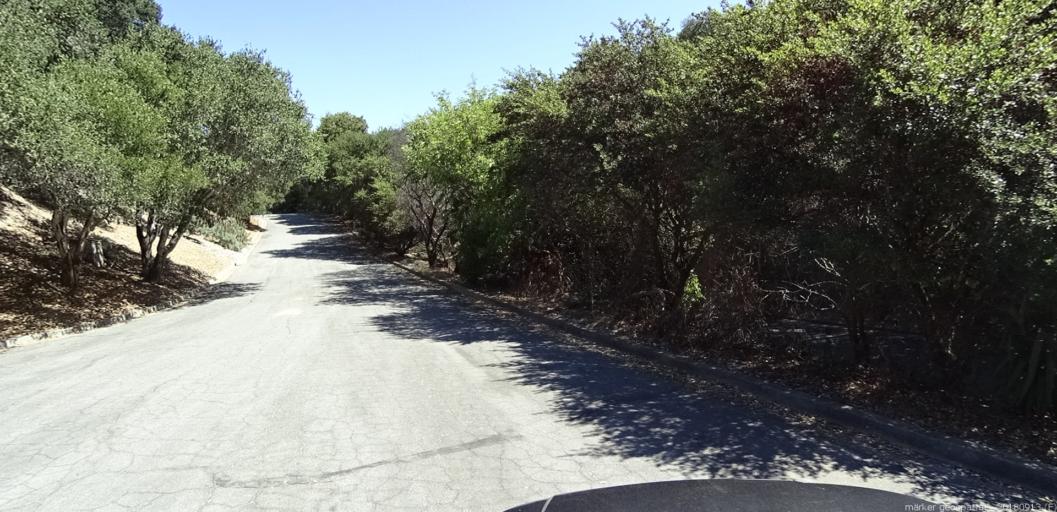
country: US
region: California
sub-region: Monterey County
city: Carmel-by-the-Sea
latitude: 36.5295
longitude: -121.8699
